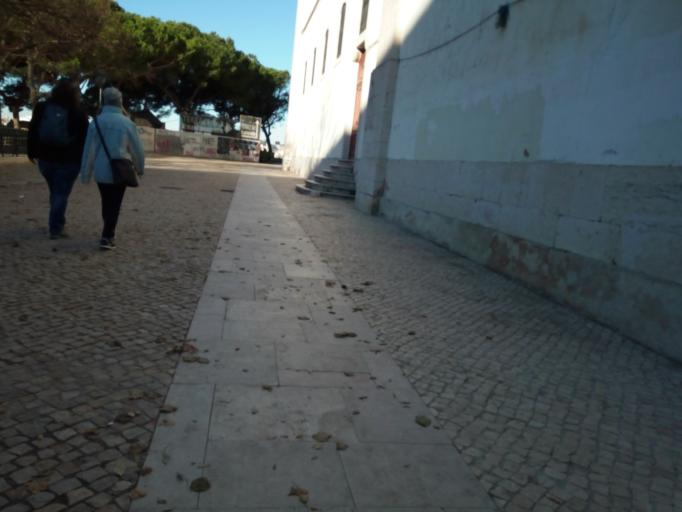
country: PT
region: Lisbon
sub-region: Lisbon
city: Lisbon
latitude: 38.7162
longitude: -9.1308
